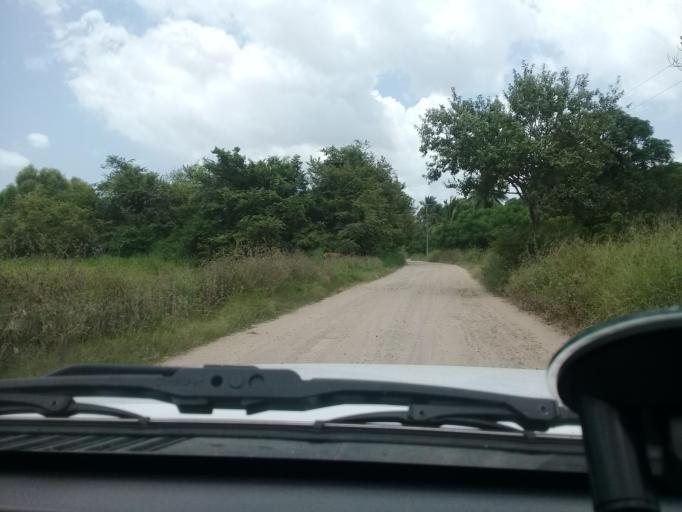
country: MX
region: Veracruz
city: Panuco
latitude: 22.1289
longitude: -98.0604
